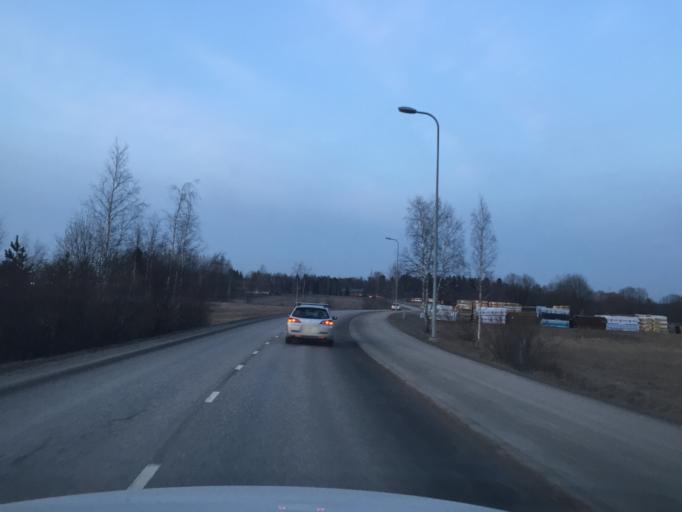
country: FI
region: Uusimaa
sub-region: Helsinki
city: Vantaa
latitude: 60.2777
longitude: 24.9782
